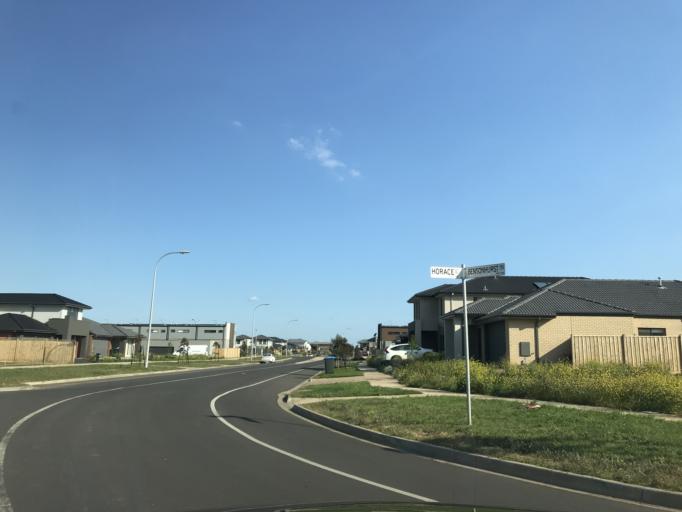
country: AU
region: Victoria
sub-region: Wyndham
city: Hoppers Crossing
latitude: -37.8829
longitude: 144.7132
